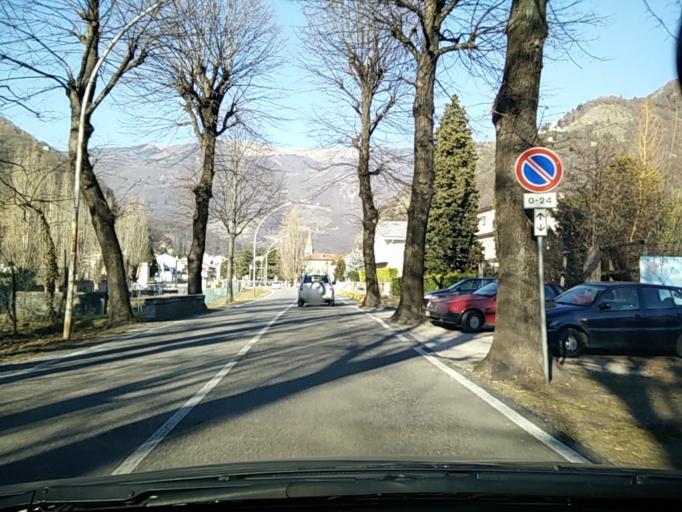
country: IT
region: Veneto
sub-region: Provincia di Treviso
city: Vittorio Veneto
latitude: 45.9959
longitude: 12.2940
